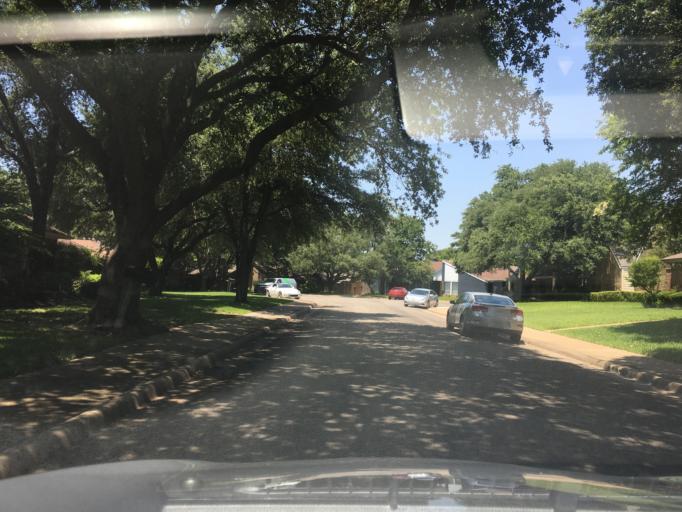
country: US
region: Texas
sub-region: Dallas County
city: Richardson
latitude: 32.9245
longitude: -96.7103
